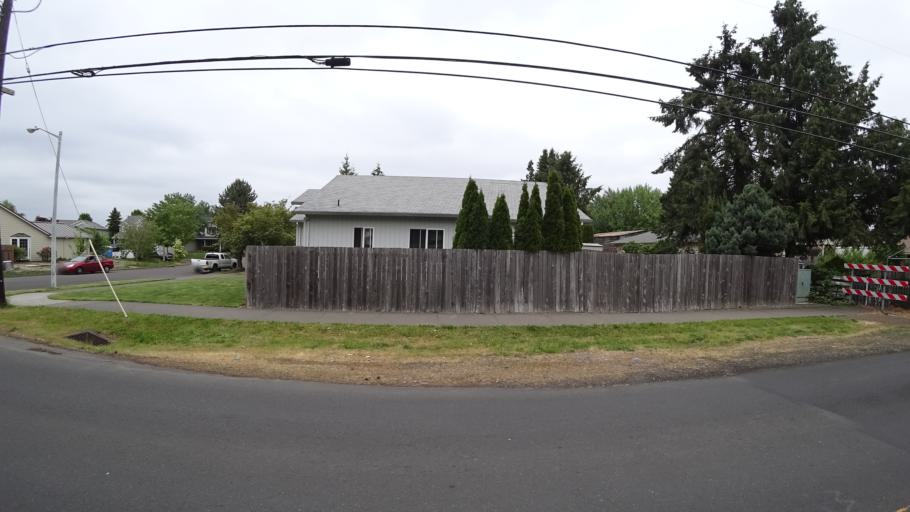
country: US
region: Oregon
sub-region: Washington County
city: Aloha
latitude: 45.5007
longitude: -122.9080
